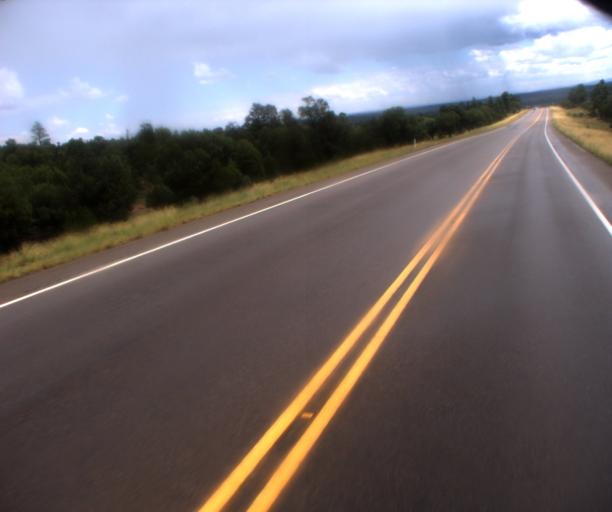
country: US
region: Arizona
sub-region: Navajo County
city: Heber-Overgaard
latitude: 34.3666
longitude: -110.3629
